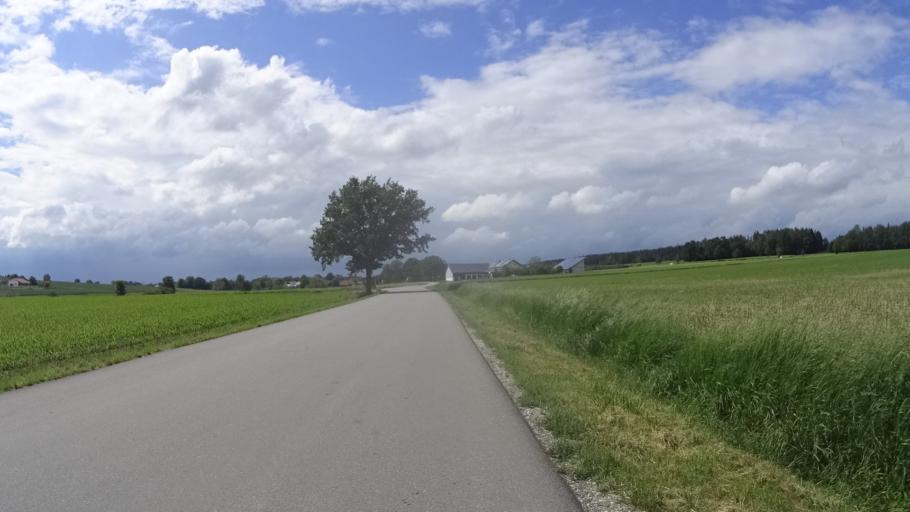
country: DE
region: Bavaria
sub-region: Lower Bavaria
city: Gangkofen
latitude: 48.4449
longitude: 12.5352
